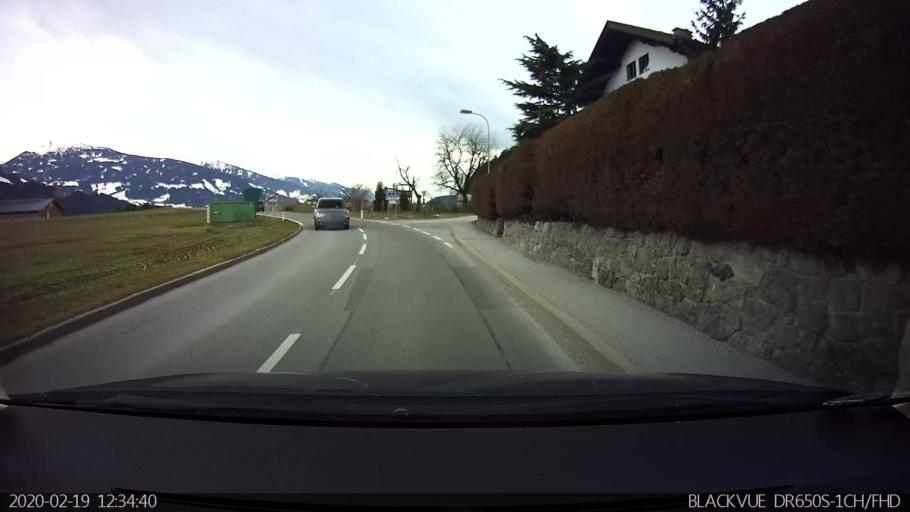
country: AT
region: Tyrol
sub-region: Politischer Bezirk Schwaz
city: Vomp
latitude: 47.3392
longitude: 11.6779
